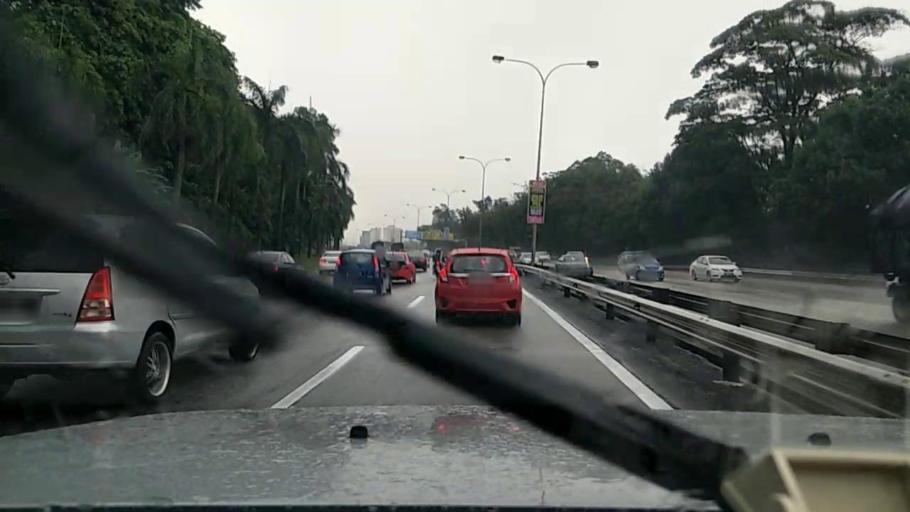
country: MY
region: Kuala Lumpur
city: Kuala Lumpur
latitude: 3.1078
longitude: 101.6922
